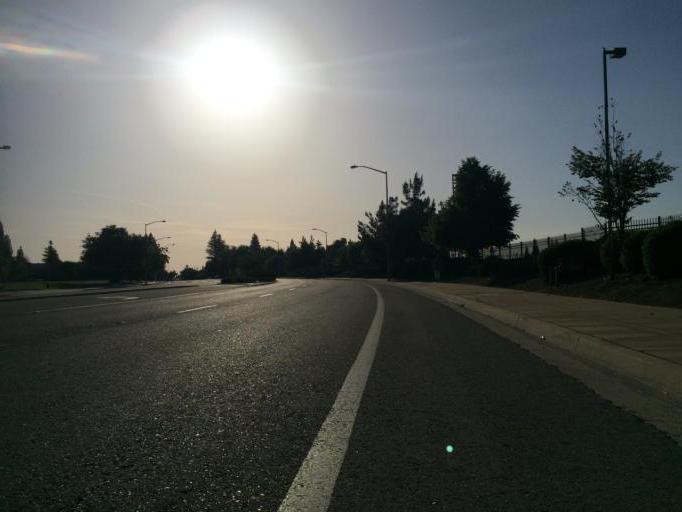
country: US
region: California
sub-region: Fresno County
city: Tarpey Village
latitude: 36.7721
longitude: -119.7243
